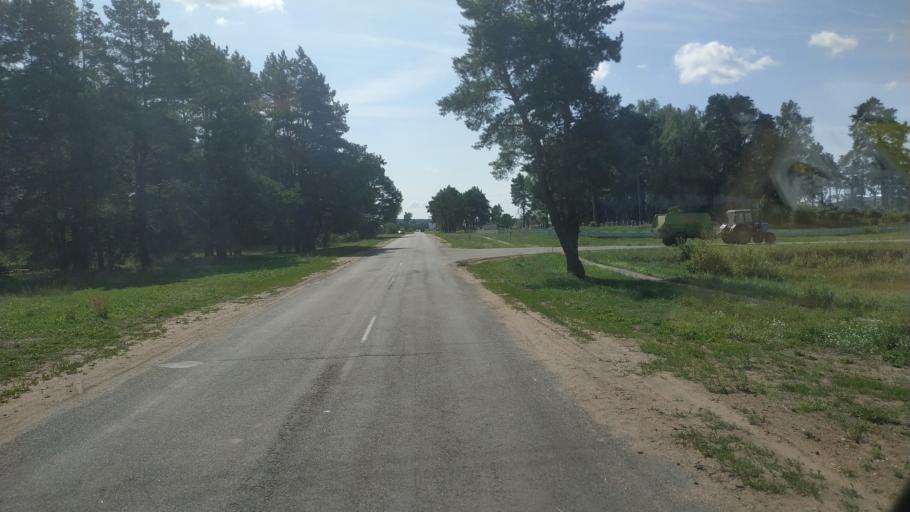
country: BY
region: Mogilev
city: Poselok Voskhod
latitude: 53.7113
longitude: 30.4969
